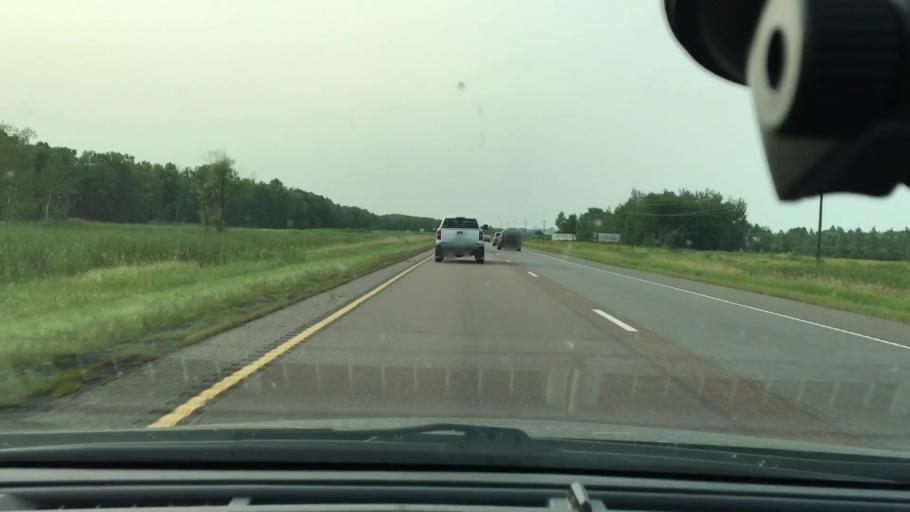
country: US
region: Minnesota
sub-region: Mille Lacs County
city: Milaca
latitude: 45.6813
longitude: -93.6360
